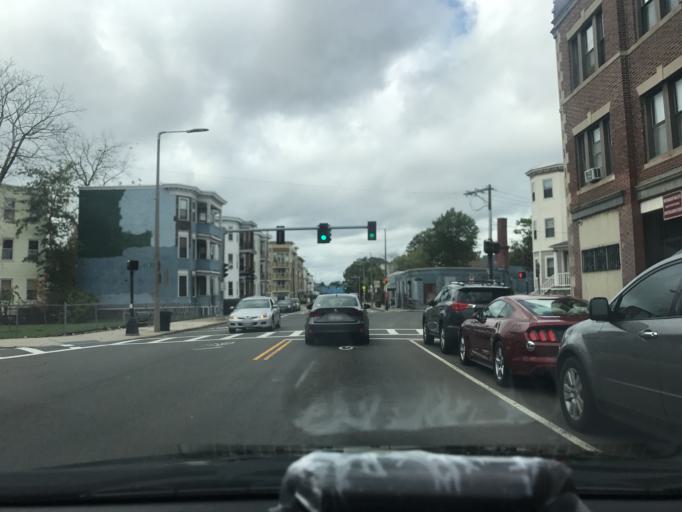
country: US
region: Massachusetts
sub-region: Norfolk County
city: Milton
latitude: 42.2910
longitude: -71.0746
